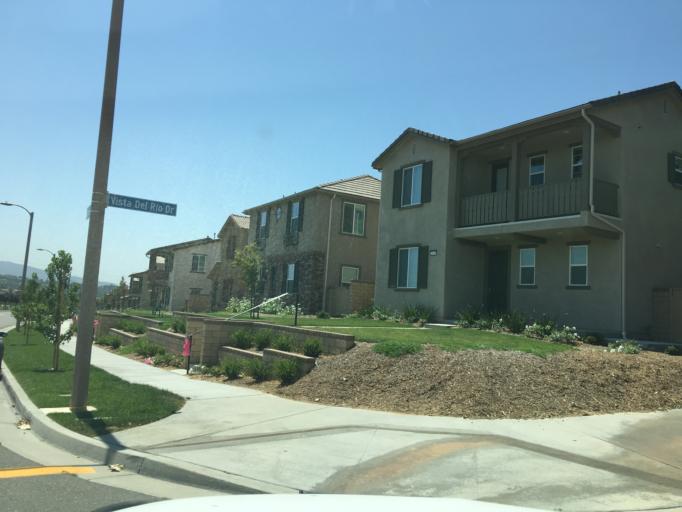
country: US
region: California
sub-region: Los Angeles County
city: Valencia
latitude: 34.4592
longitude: -118.5622
